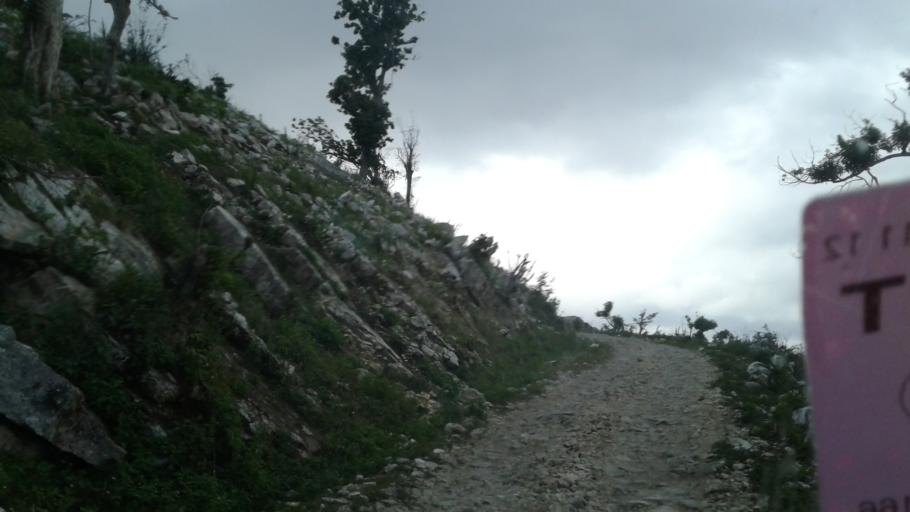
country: HT
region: Grandans
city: Jeremie
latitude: 18.4978
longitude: -74.0979
